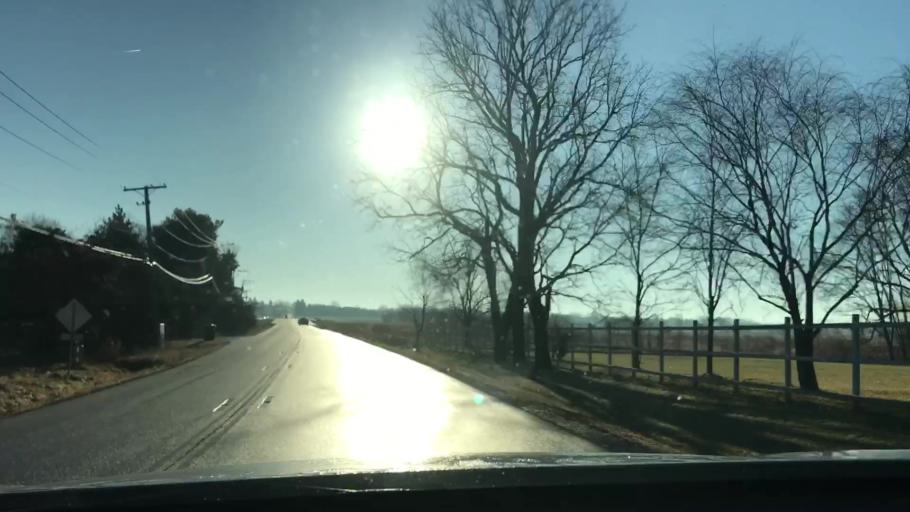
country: US
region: Illinois
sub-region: Kane County
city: Pingree Grove
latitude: 42.0903
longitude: -88.3976
